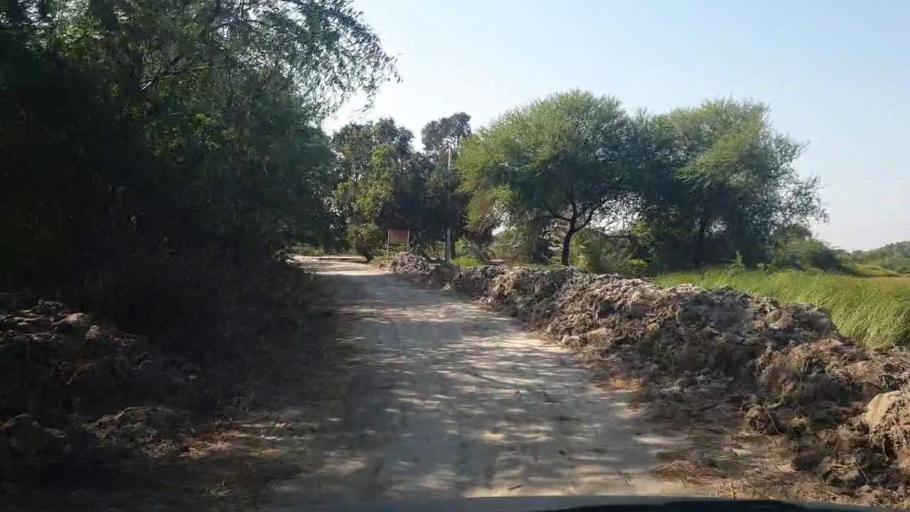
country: PK
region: Sindh
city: Badin
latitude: 24.5803
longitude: 68.7941
